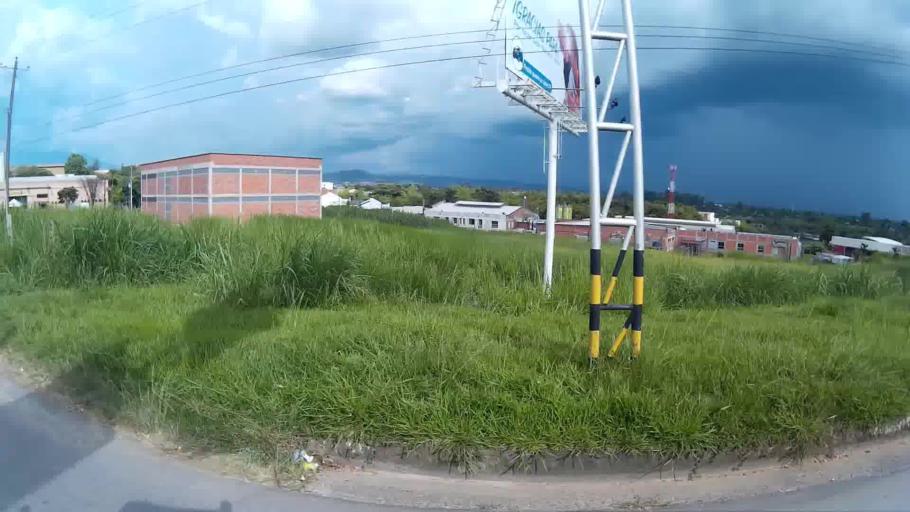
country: CO
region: Risaralda
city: Pereira
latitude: 4.8135
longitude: -75.7652
